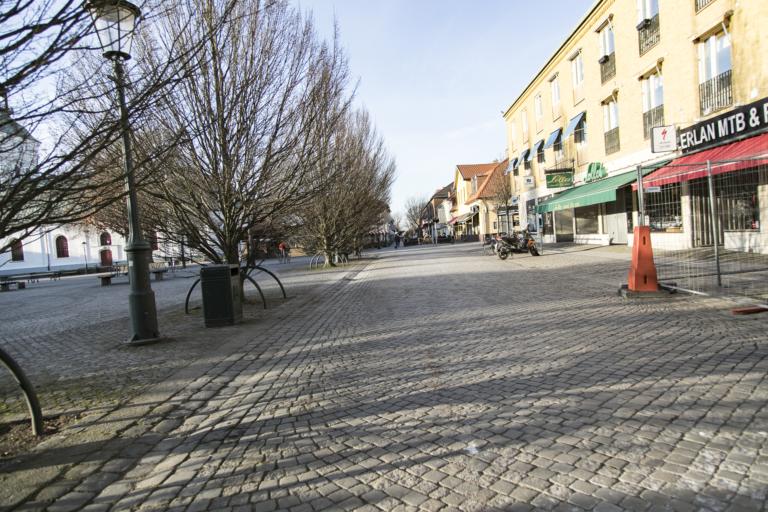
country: SE
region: Halland
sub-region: Varbergs Kommun
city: Varberg
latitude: 57.1051
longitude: 12.2513
